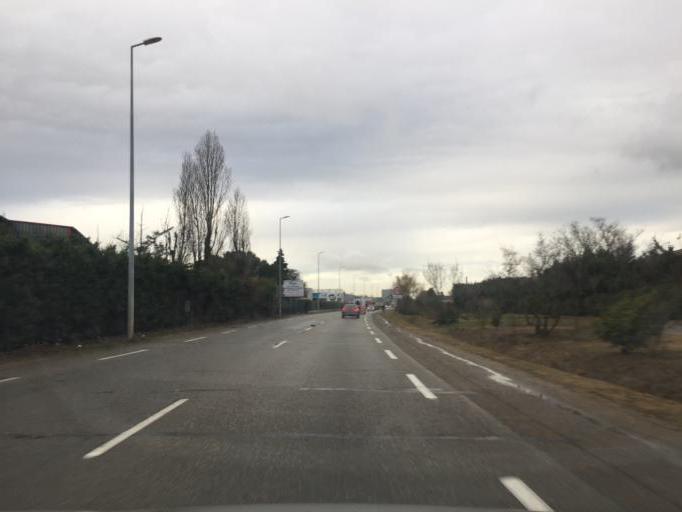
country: FR
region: Rhone-Alpes
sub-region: Departement du Rhone
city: Chassieu
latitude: 45.7326
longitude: 4.9713
